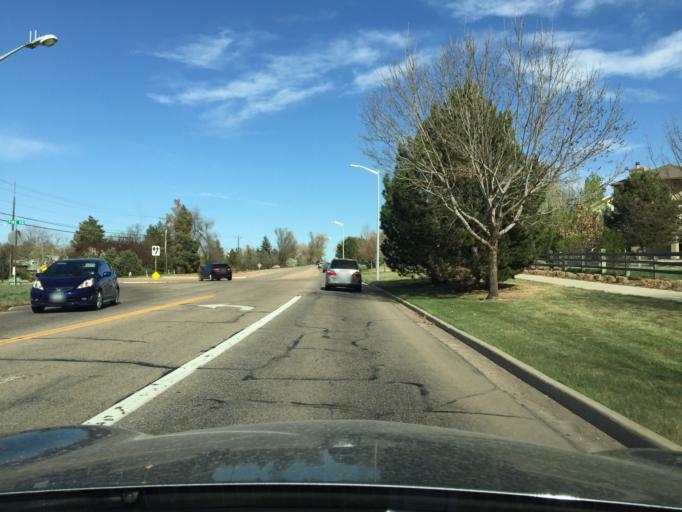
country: US
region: Colorado
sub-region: Boulder County
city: Longmont
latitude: 40.1378
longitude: -105.1138
